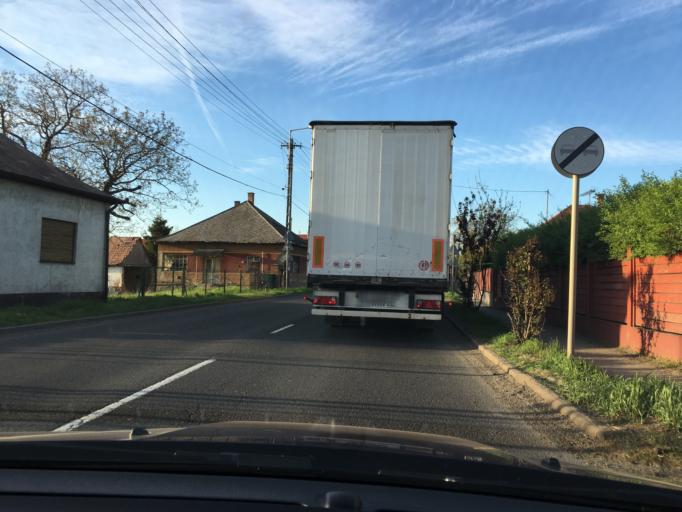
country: HU
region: Hajdu-Bihar
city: Mikepercs
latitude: 47.4399
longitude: 21.6314
